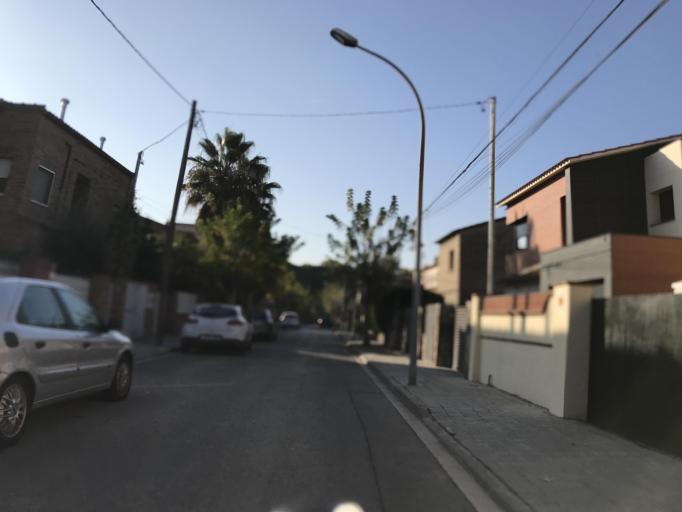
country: ES
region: Catalonia
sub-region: Provincia de Barcelona
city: Mollet del Valles
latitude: 41.5575
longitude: 2.2198
